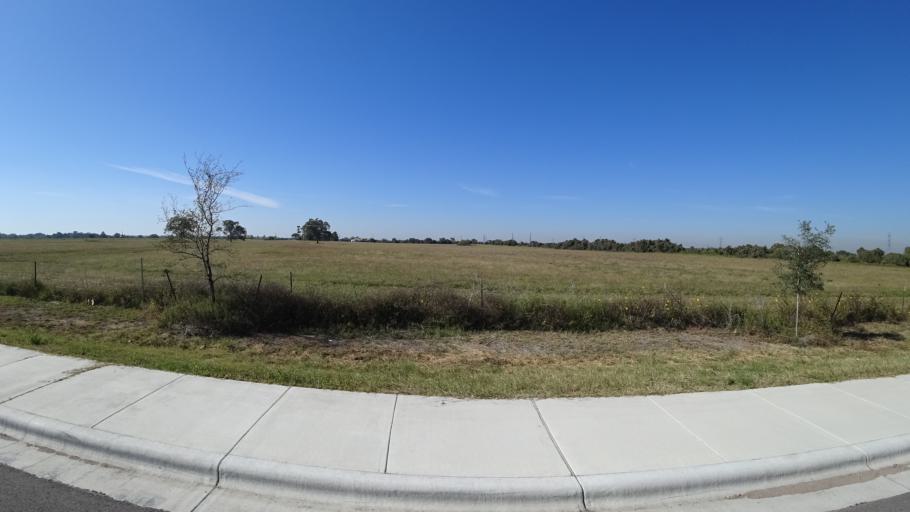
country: US
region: Texas
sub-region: Travis County
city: Hornsby Bend
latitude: 30.2484
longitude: -97.5959
